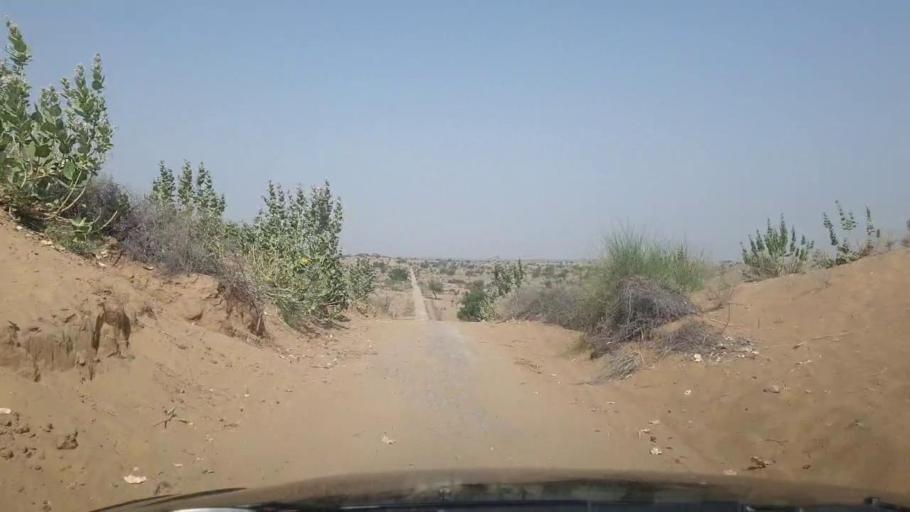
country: PK
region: Sindh
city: Islamkot
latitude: 25.0578
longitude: 70.2102
